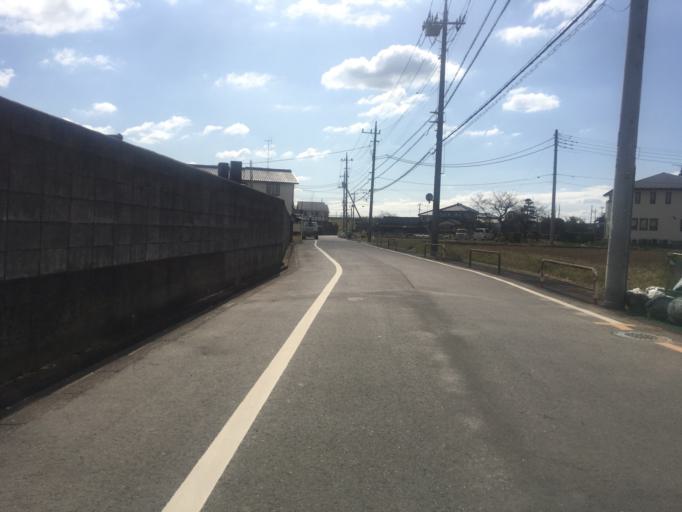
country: JP
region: Saitama
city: Shiki
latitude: 35.8697
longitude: 139.5932
